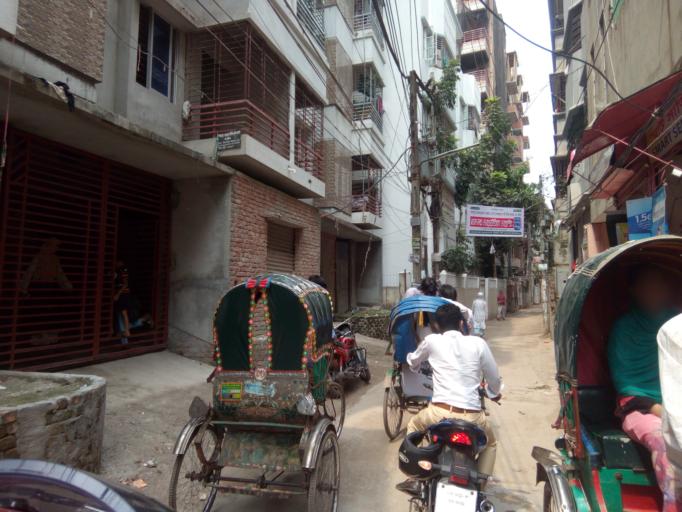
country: BD
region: Dhaka
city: Paltan
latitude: 23.7335
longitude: 90.4333
